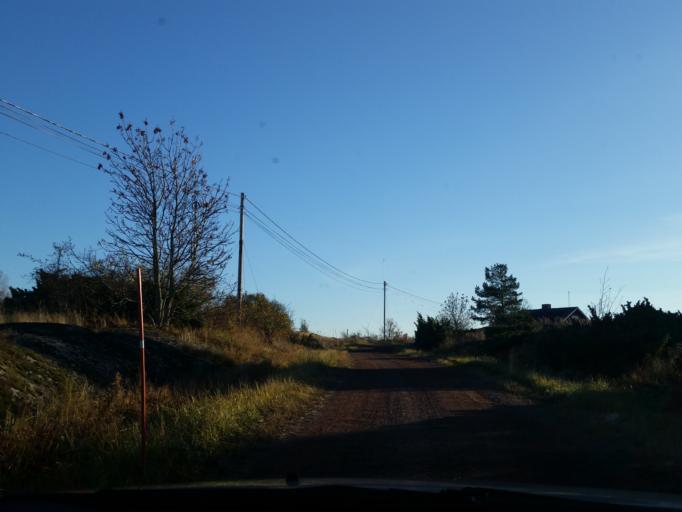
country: AX
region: Alands skaergard
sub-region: Braendoe
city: Braendoe
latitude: 60.4530
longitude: 20.9355
